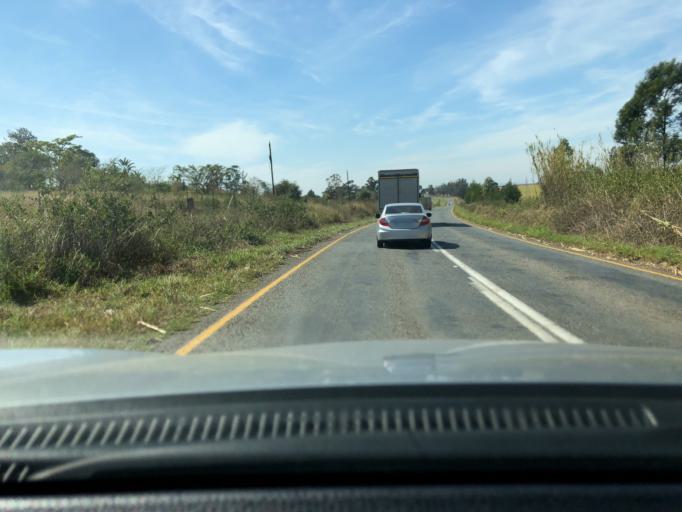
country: ZA
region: KwaZulu-Natal
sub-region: uMgungundlovu District Municipality
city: Camperdown
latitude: -29.7304
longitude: 30.4423
